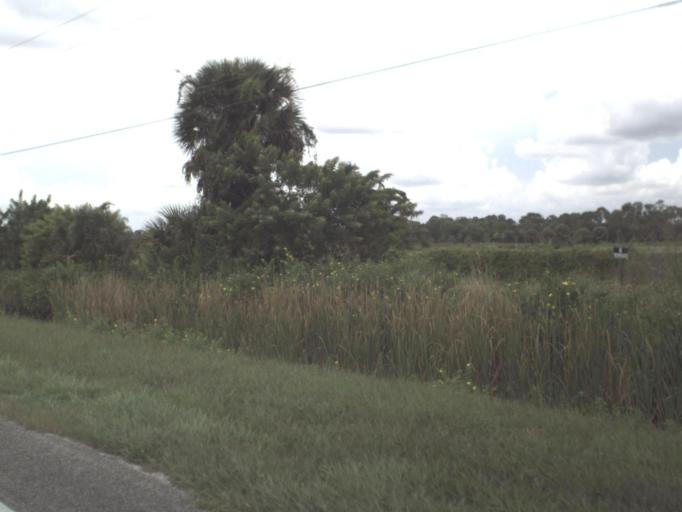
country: US
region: Florida
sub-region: Lee County
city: Olga
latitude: 26.7154
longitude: -81.6817
